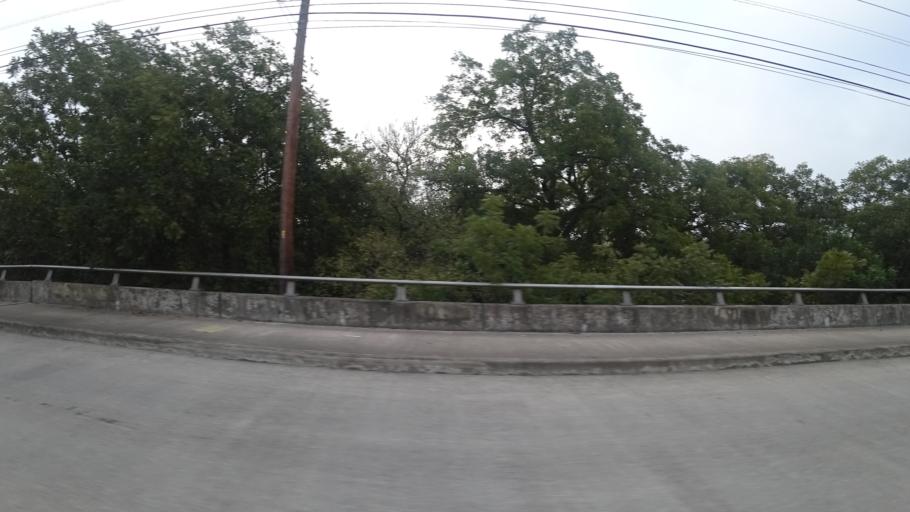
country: US
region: Texas
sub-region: Travis County
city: Wells Branch
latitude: 30.3752
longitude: -97.6604
